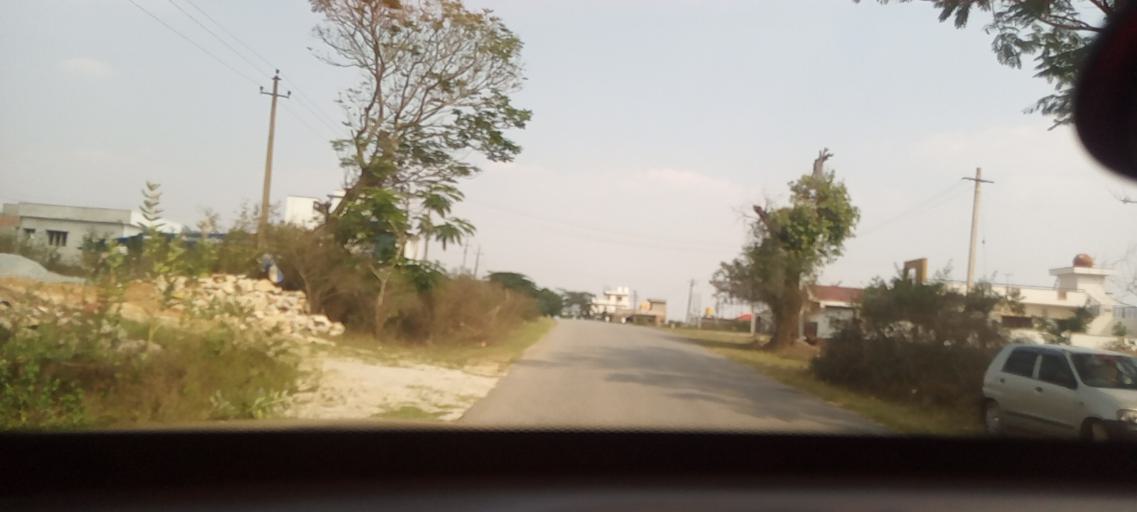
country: IN
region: Karnataka
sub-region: Hassan
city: Belur
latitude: 13.1746
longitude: 75.8531
